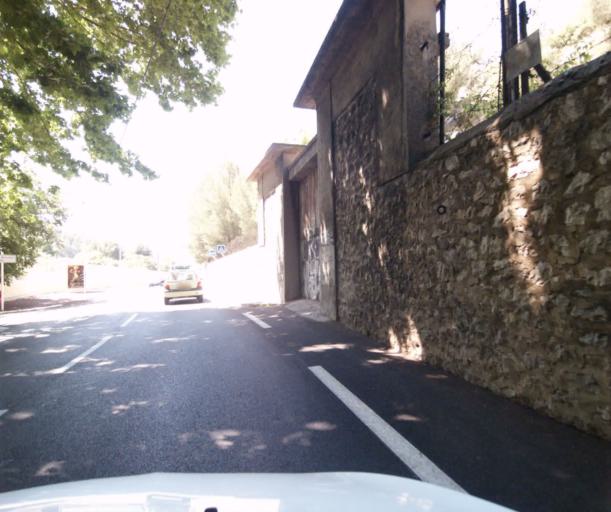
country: FR
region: Provence-Alpes-Cote d'Azur
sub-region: Departement du Var
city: Le Revest-les-Eaux
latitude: 43.1552
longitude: 5.9156
